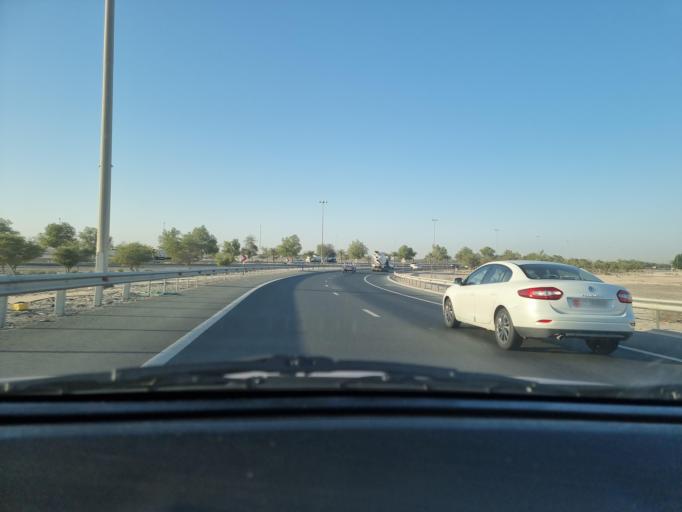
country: AE
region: Abu Dhabi
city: Abu Dhabi
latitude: 24.4151
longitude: 54.7112
